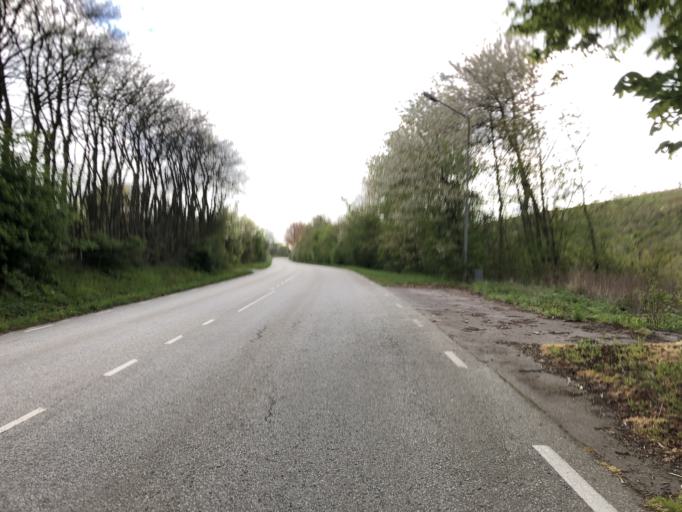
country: SE
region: Skane
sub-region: Lunds Kommun
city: Genarp
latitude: 55.6581
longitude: 13.3819
